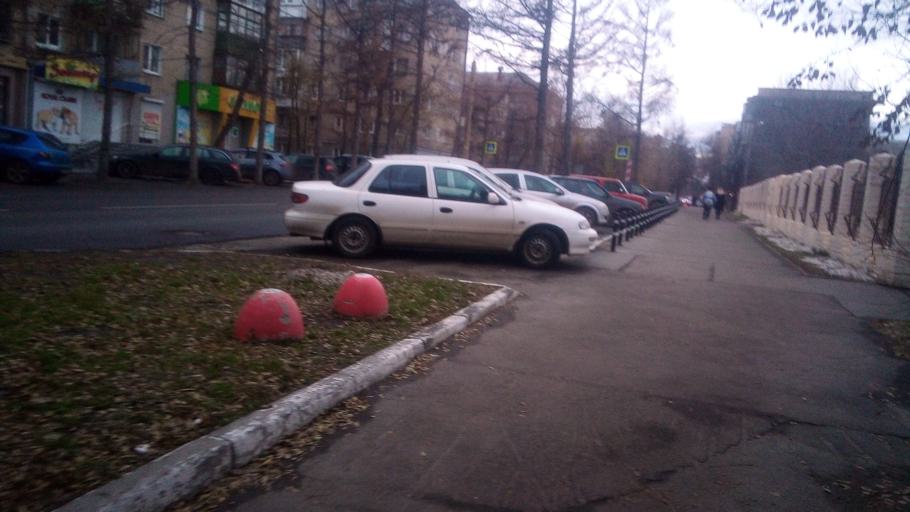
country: RU
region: Chelyabinsk
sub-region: Gorod Chelyabinsk
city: Chelyabinsk
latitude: 55.1578
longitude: 61.3847
